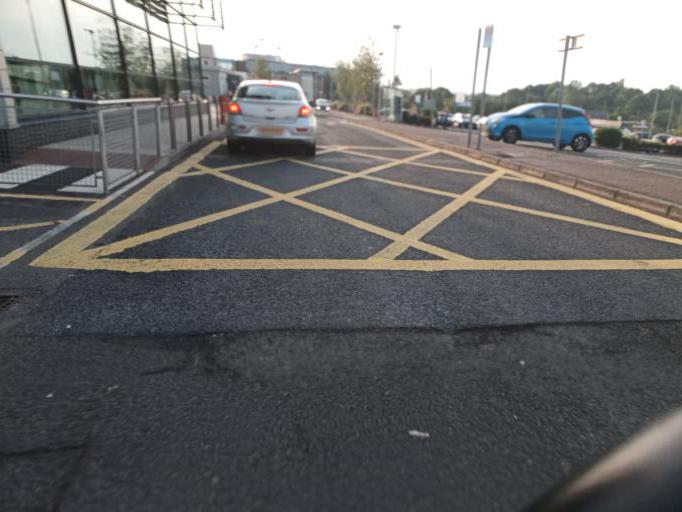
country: GB
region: Northern Ireland
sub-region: Castlereagh District
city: Dundonald
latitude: 54.5959
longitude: -5.8118
